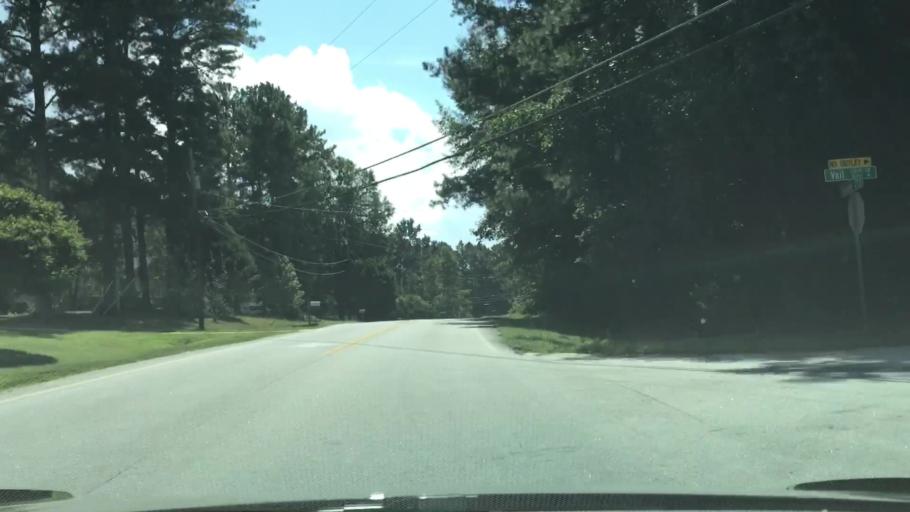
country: US
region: Georgia
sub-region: Gwinnett County
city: Snellville
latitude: 33.8626
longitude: -84.0495
